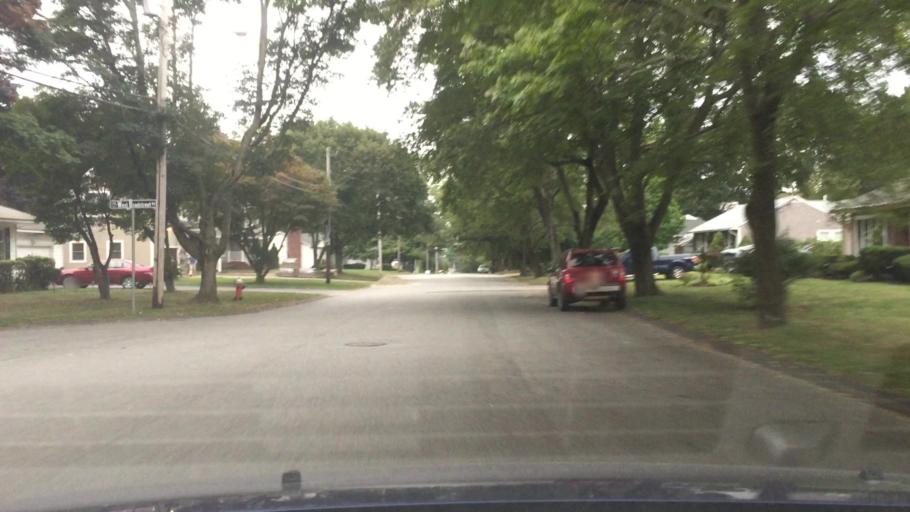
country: US
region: Massachusetts
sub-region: Essex County
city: North Andover
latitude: 42.6961
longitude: -71.1289
